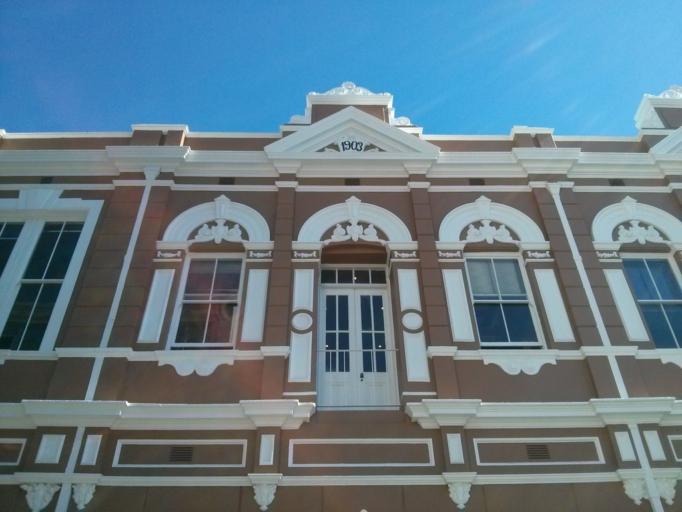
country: ZA
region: Western Cape
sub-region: City of Cape Town
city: Cape Town
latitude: -33.9208
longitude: 18.4156
